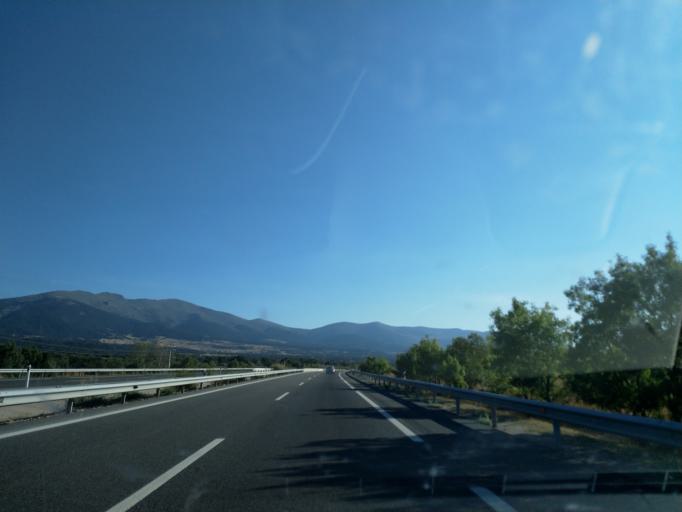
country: ES
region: Castille and Leon
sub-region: Provincia de Segovia
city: Segovia
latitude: 40.8829
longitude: -4.1174
